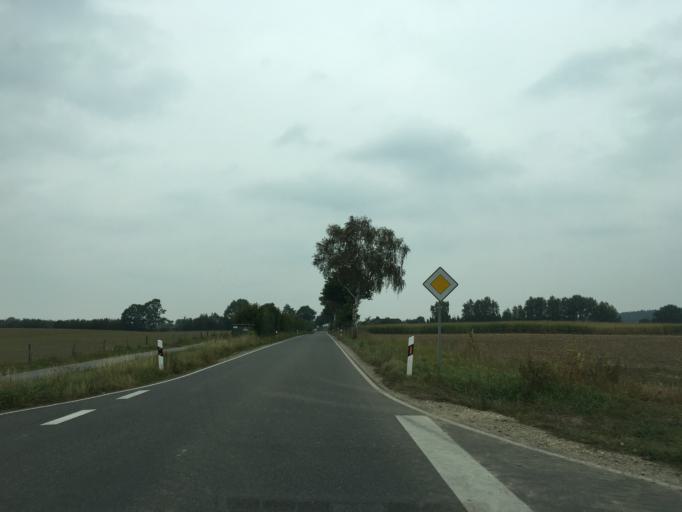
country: DE
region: Schleswig-Holstein
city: Seedorf
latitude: 53.6294
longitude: 10.8432
